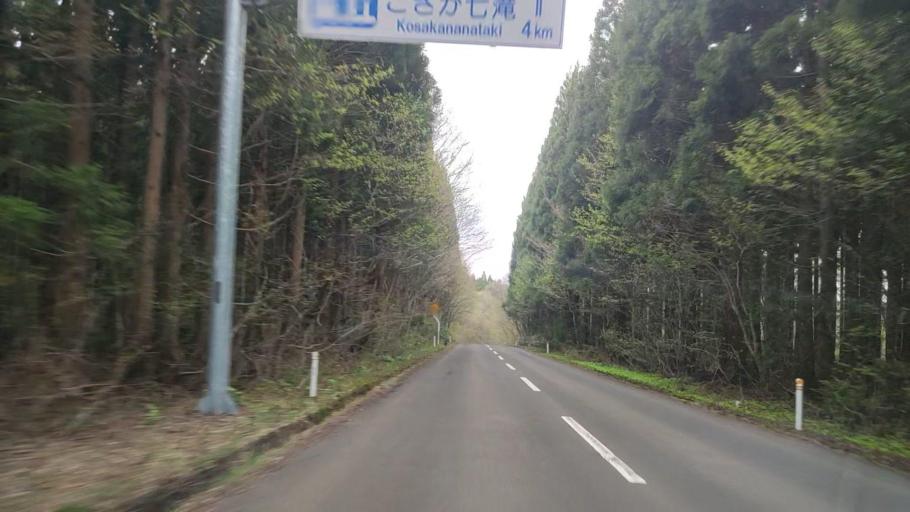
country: JP
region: Akita
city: Hanawa
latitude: 40.3859
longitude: 140.7927
